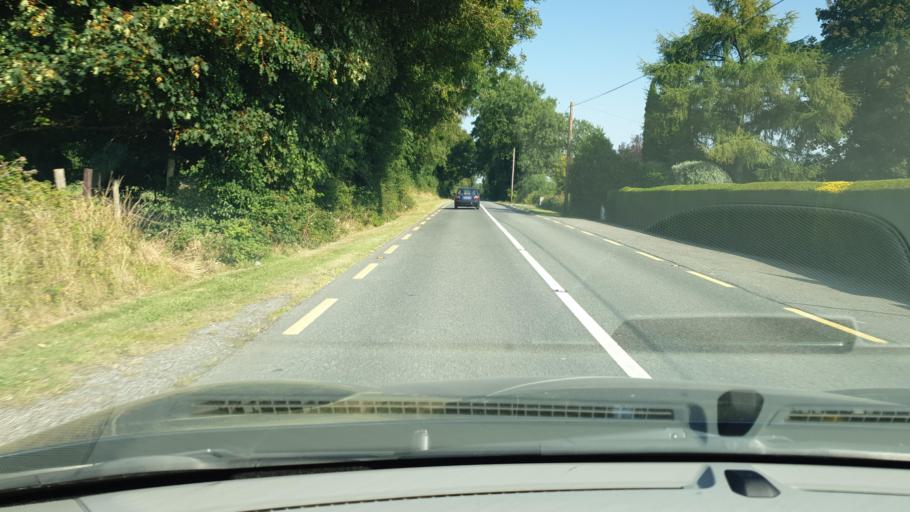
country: IE
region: Leinster
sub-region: An Mhi
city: Trim
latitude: 53.6326
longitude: -6.8046
